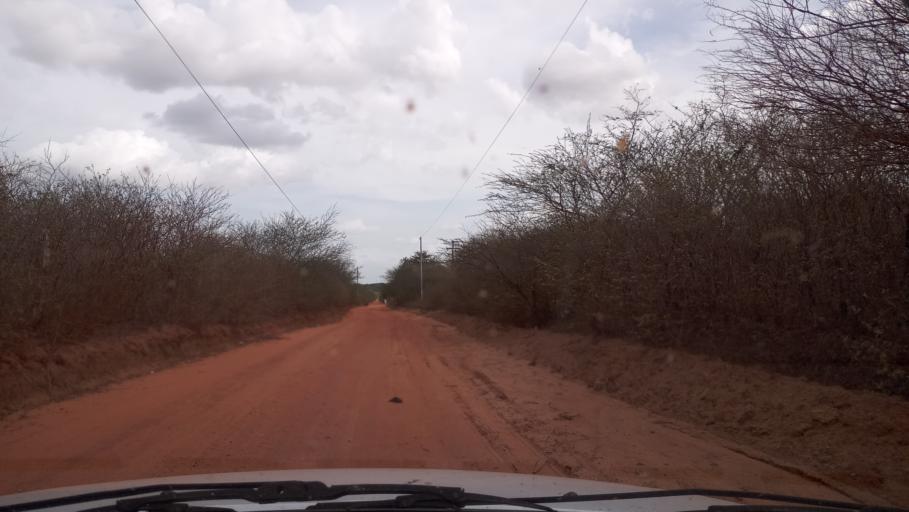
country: BR
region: Rio Grande do Norte
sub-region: Joao Camara
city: Joao Camara
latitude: -5.4969
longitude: -35.8268
